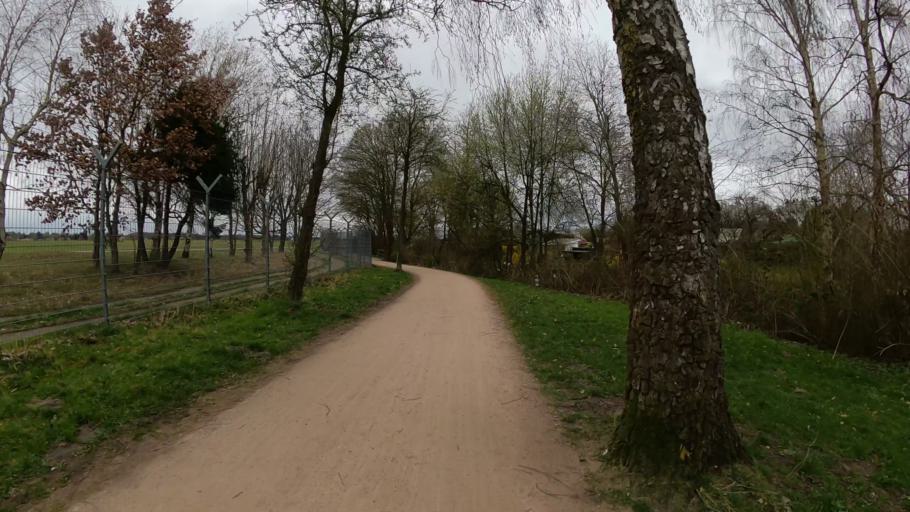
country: DE
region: Hamburg
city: Hamburg-Nord
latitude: 53.6165
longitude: 9.9672
